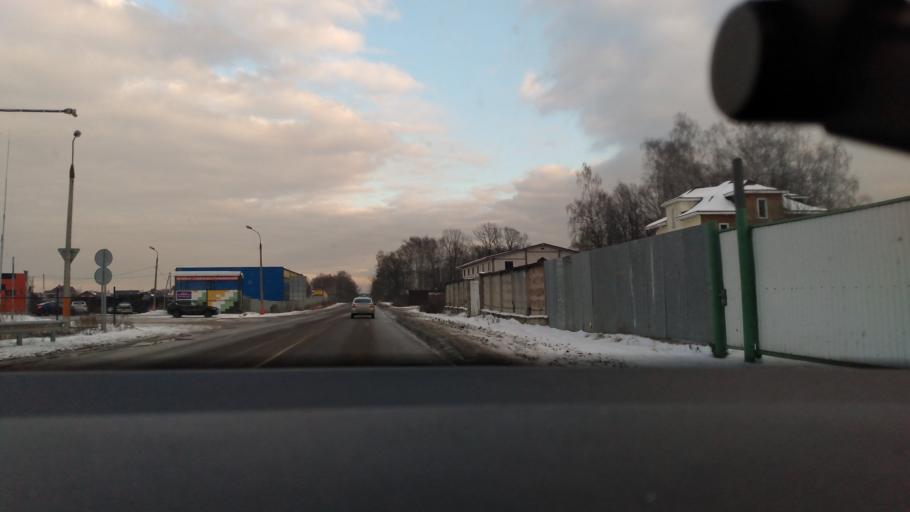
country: RU
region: Moskovskaya
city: Rodniki
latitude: 55.6957
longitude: 38.0562
